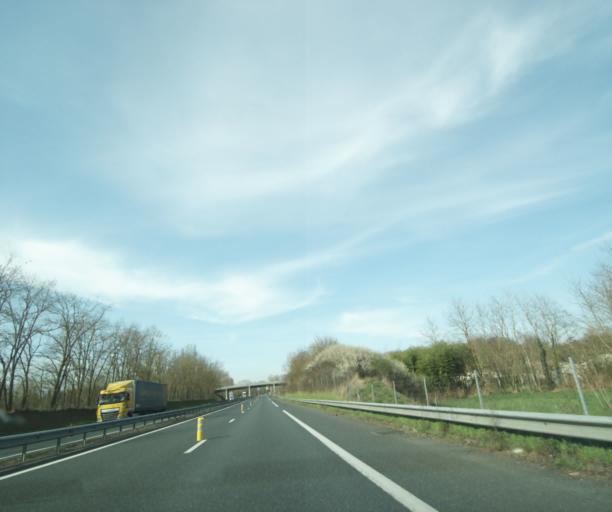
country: FR
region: Centre
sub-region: Departement du Cher
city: Vierzon
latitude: 47.2247
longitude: 2.0393
